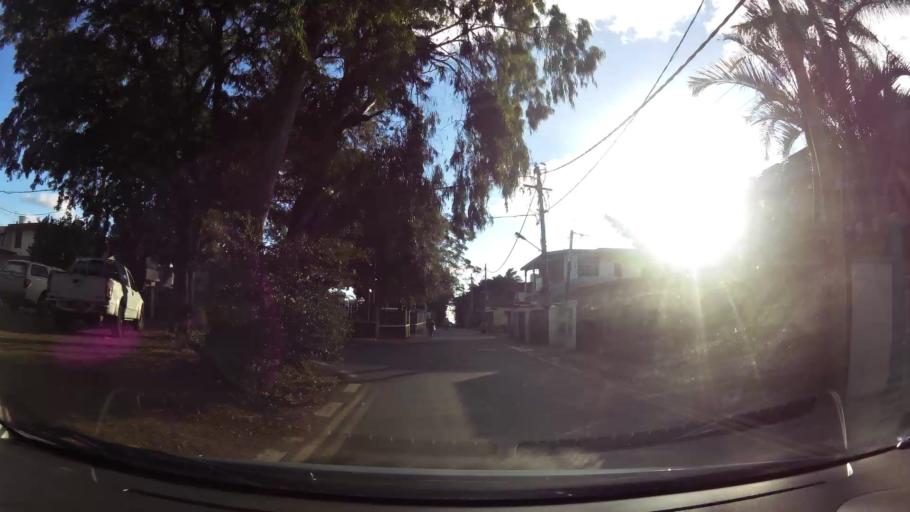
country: MU
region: Black River
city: Petite Riviere
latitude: -20.2213
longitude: 57.4638
